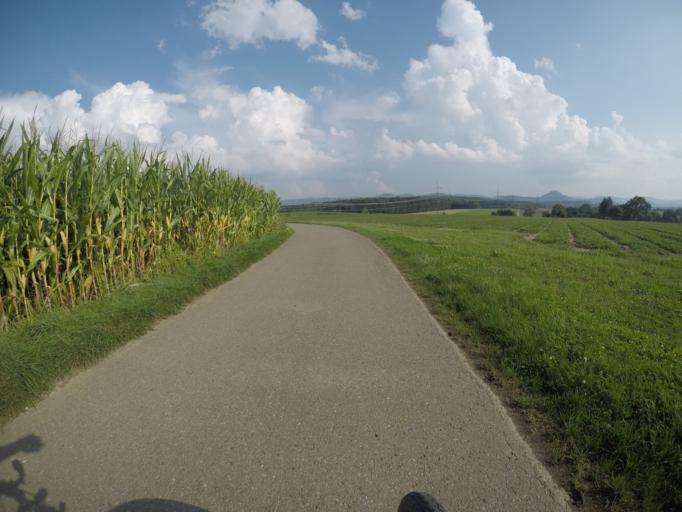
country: DE
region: Baden-Wuerttemberg
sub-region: Tuebingen Region
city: Pliezhausen
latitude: 48.5547
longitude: 9.2372
